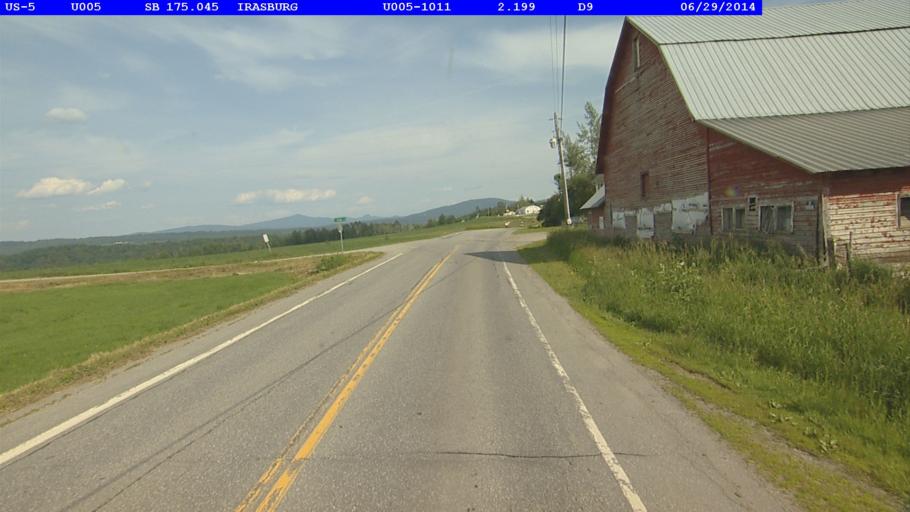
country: US
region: Vermont
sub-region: Orleans County
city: Newport
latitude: 44.8280
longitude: -72.2424
